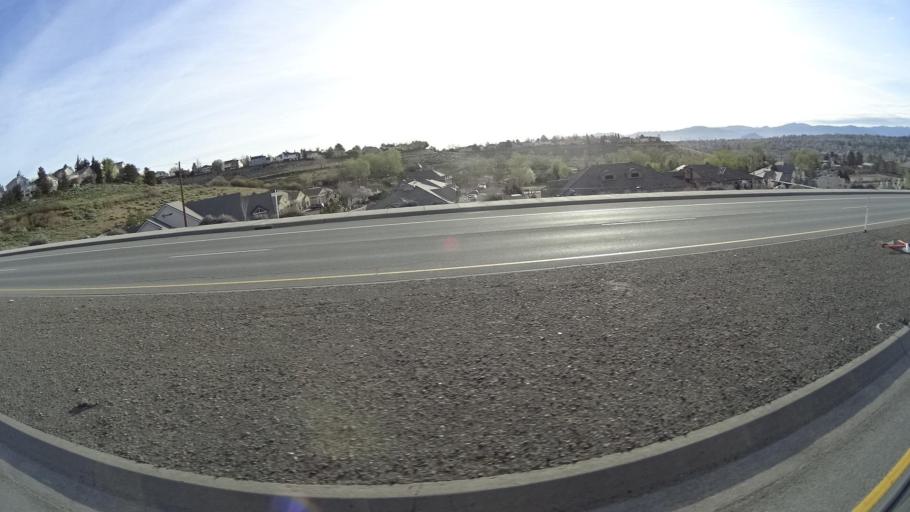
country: US
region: Nevada
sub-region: Washoe County
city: Reno
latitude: 39.5176
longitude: -119.8610
